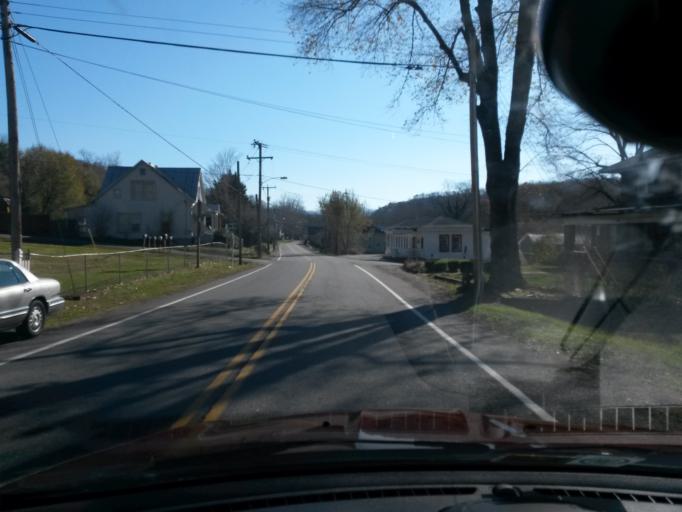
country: US
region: Virginia
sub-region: Botetourt County
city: Fincastle
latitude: 37.6402
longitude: -79.8007
